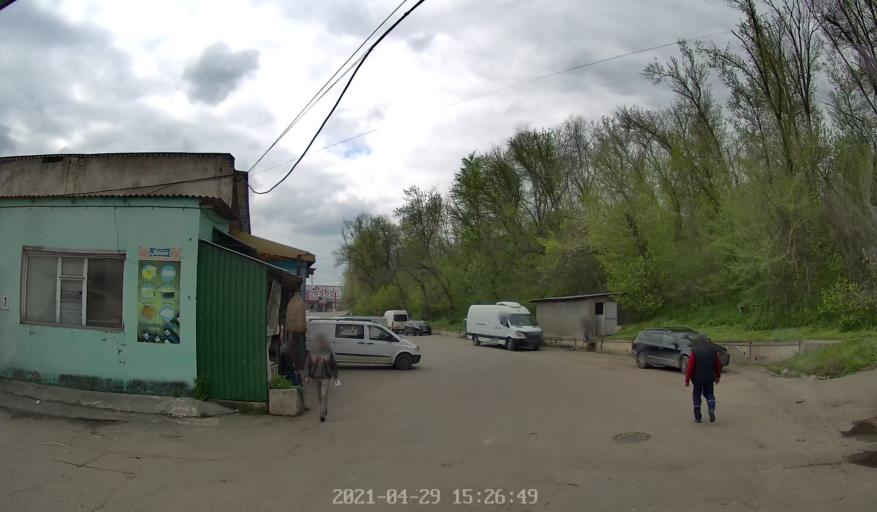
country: MD
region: Chisinau
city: Chisinau
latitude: 47.0510
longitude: 28.8188
